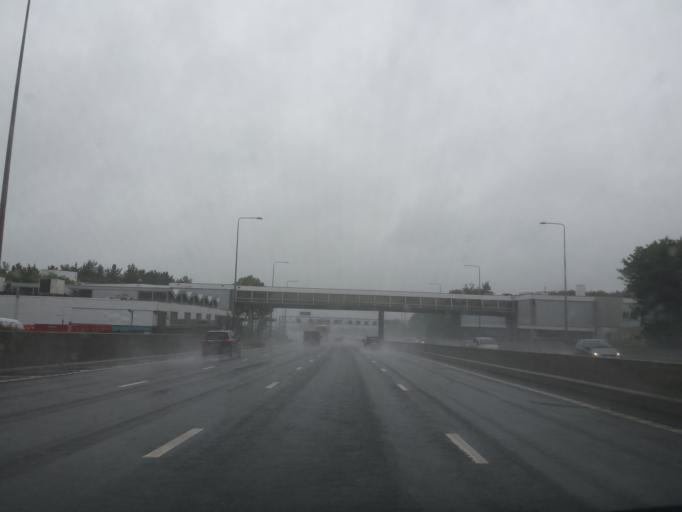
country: GB
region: England
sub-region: Nottinghamshire
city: Kimberley
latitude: 52.9622
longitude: -1.2671
